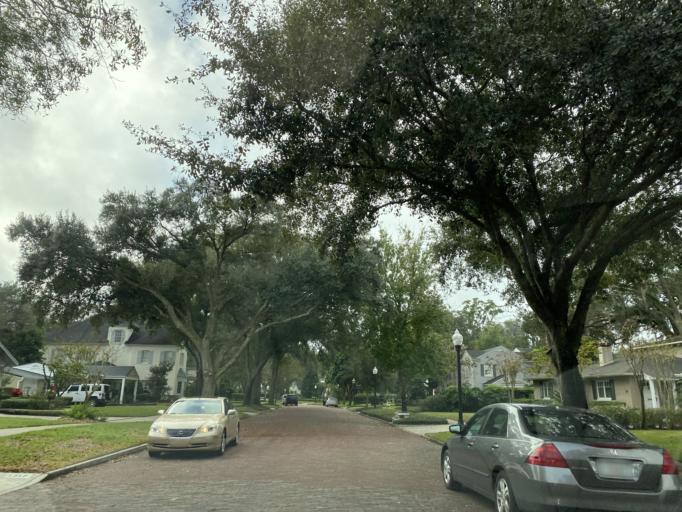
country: US
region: Florida
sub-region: Orange County
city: Fairview Shores
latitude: 28.5635
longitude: -81.3945
